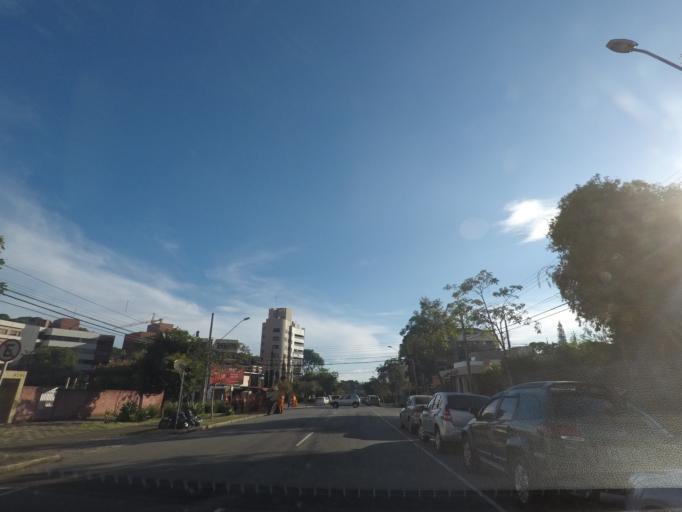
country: BR
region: Parana
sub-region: Curitiba
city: Curitiba
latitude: -25.4496
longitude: -49.2980
